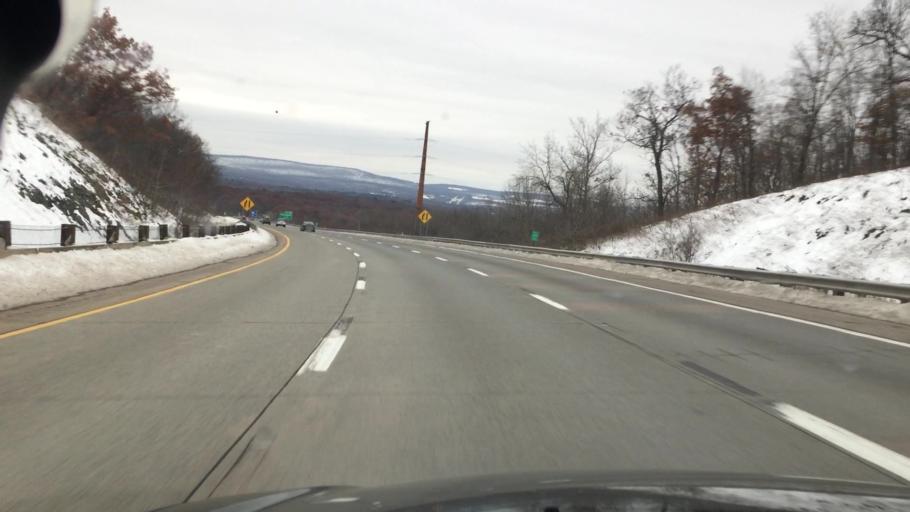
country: US
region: Pennsylvania
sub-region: Luzerne County
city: Nanticoke
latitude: 41.1701
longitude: -75.9574
